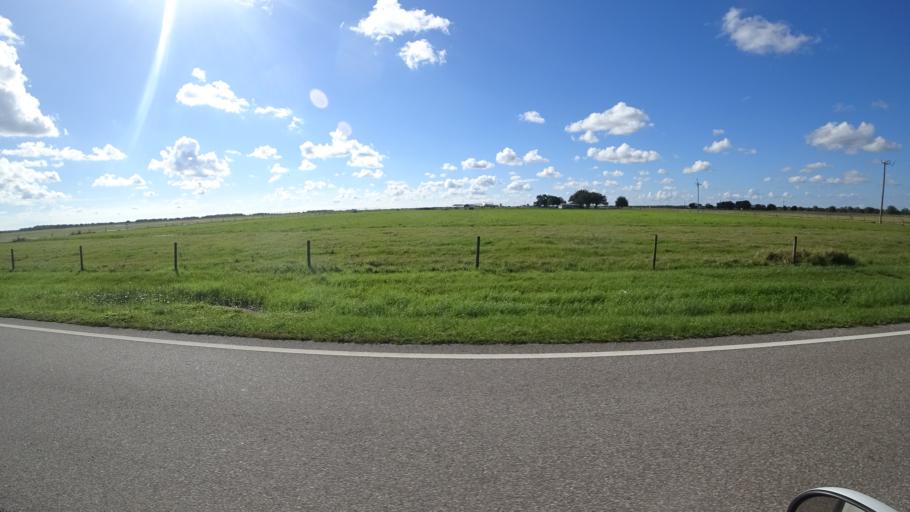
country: US
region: Florida
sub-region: Sarasota County
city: Lake Sarasota
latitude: 27.3692
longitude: -82.2683
